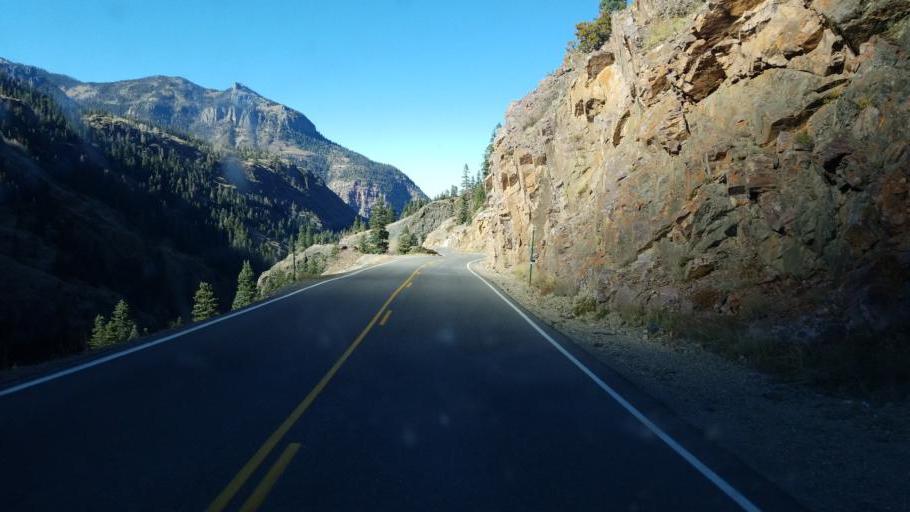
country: US
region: Colorado
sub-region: Ouray County
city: Ouray
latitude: 37.9954
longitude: -107.6572
